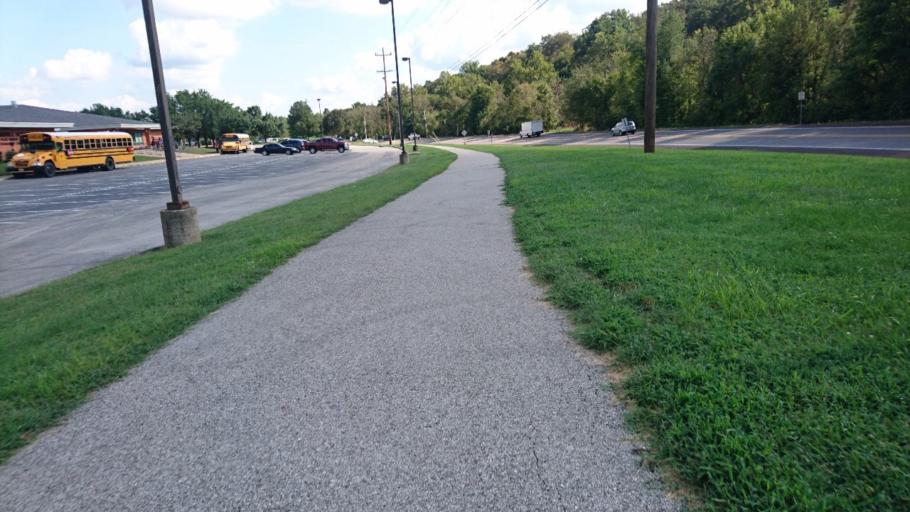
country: US
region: Missouri
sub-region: Saint Louis County
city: Wildwood
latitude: 38.5521
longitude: -90.6405
